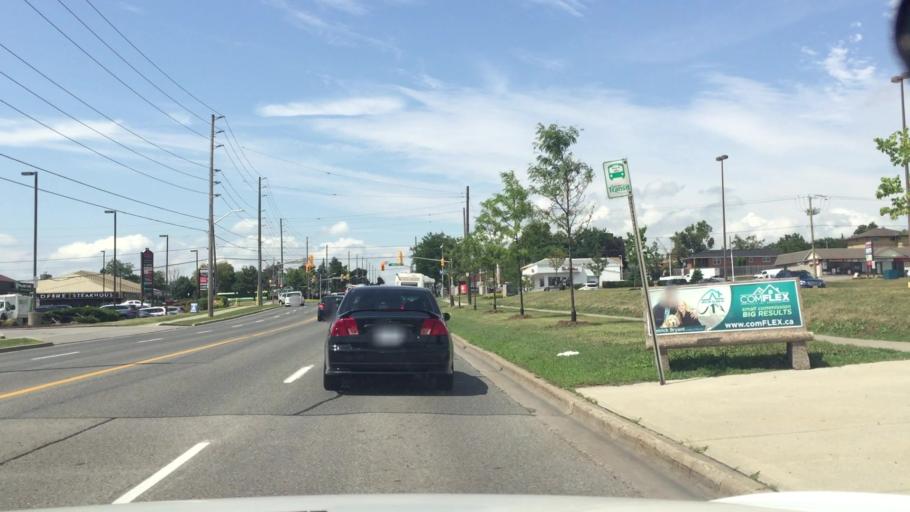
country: CA
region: Ontario
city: Oshawa
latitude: 43.8920
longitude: -78.8828
